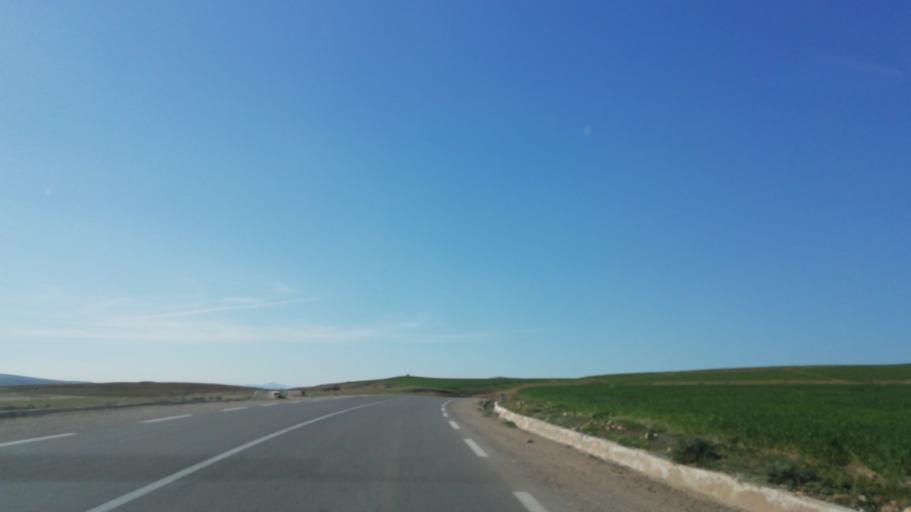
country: DZ
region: Mascara
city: Oued el Abtal
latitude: 35.4478
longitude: 0.8145
